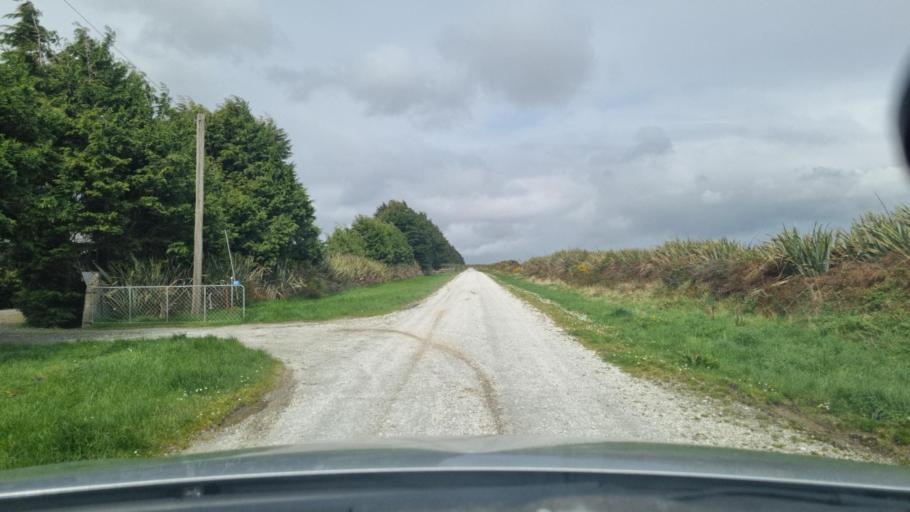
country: NZ
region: Southland
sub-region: Invercargill City
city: Bluff
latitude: -46.5139
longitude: 168.3563
